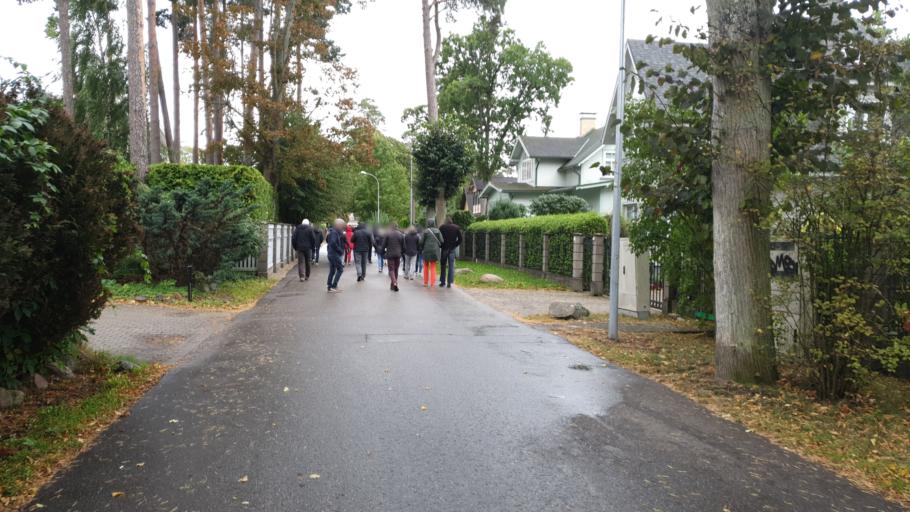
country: LV
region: Jurmala
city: Jurmala
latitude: 56.9762
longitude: 23.8090
